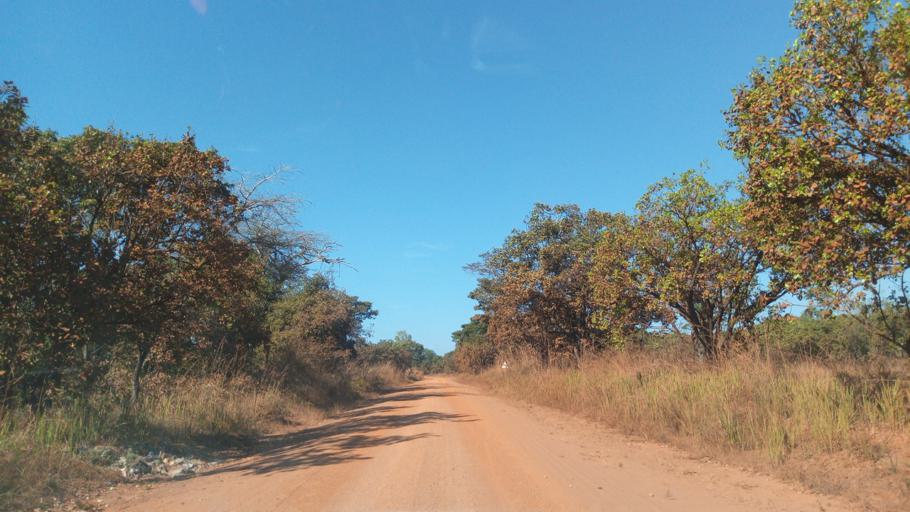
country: ZM
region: Luapula
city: Mwense
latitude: -10.6565
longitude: 28.4079
